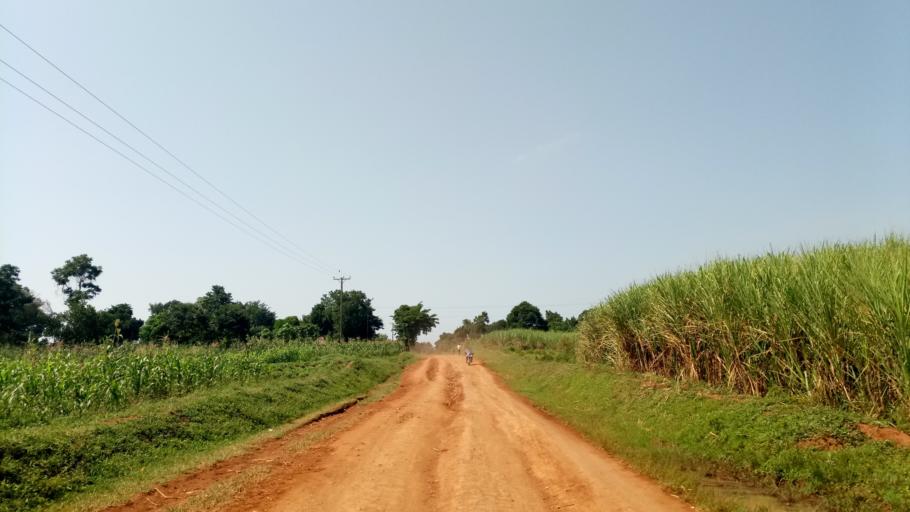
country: UG
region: Eastern Region
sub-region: Kaliro District
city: Kaliro
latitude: 0.9724
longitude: 33.4620
